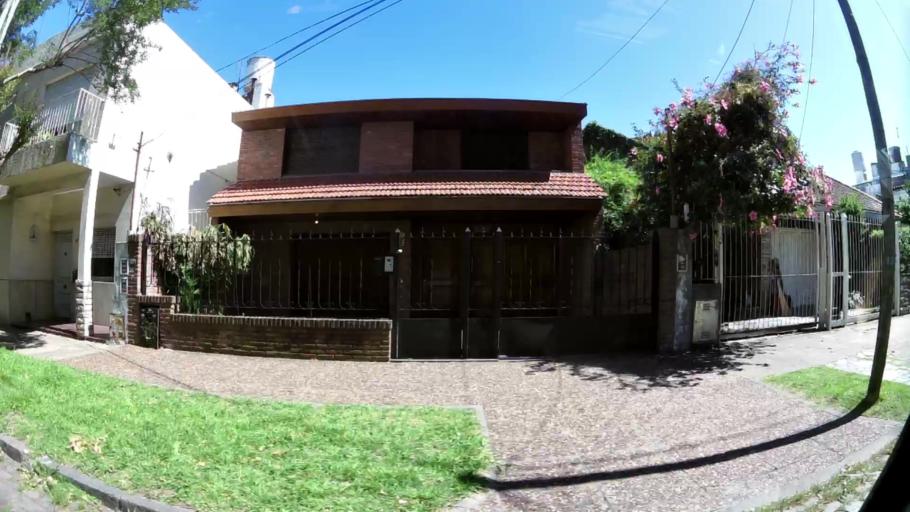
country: AR
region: Buenos Aires
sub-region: Partido de Vicente Lopez
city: Olivos
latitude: -34.5194
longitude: -58.5026
